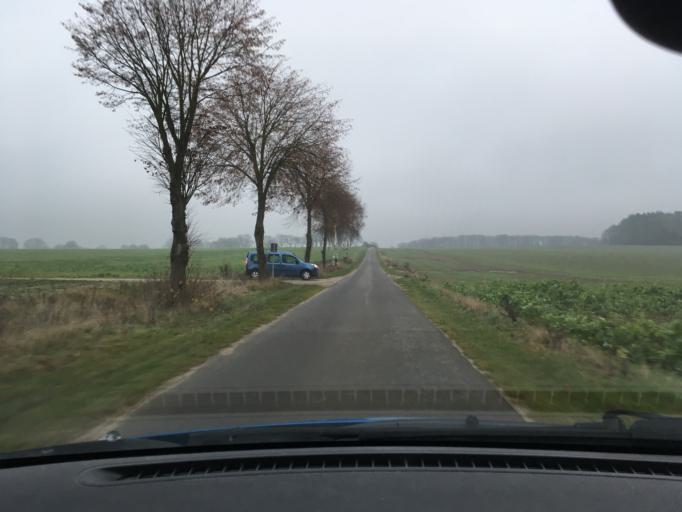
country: DE
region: Lower Saxony
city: Amelinghausen
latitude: 53.1114
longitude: 10.2014
